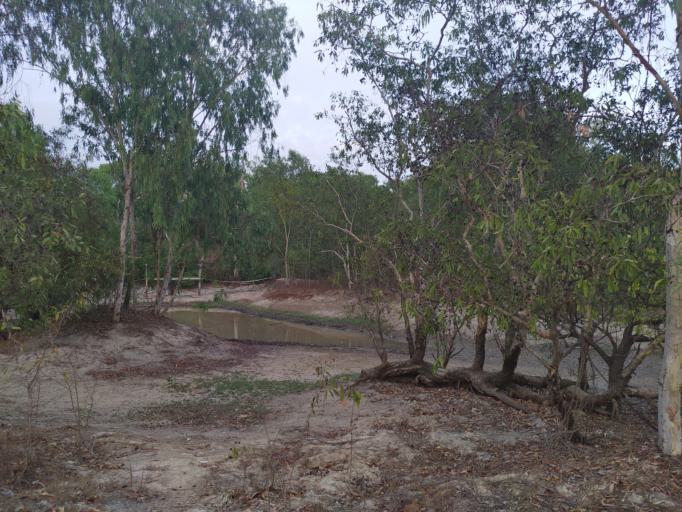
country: AU
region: Northern Territory
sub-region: Litchfield
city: McMinns Lagoon
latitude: -12.9074
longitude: 131.6489
